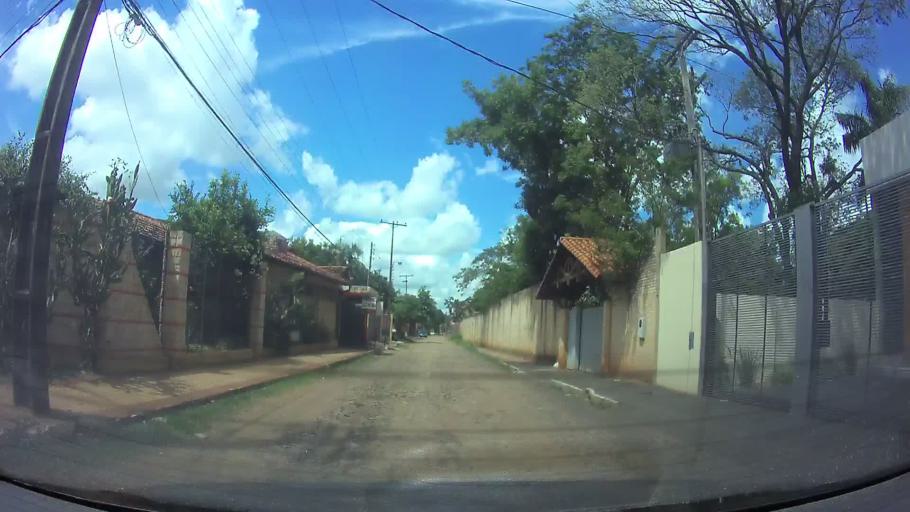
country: PY
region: Central
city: Fernando de la Mora
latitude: -25.3161
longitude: -57.5257
